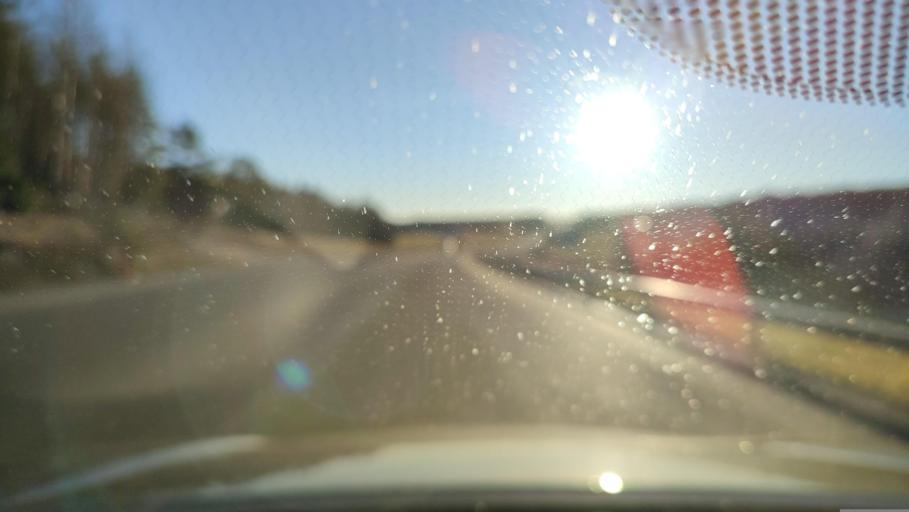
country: SE
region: Vaesterbotten
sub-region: Robertsfors Kommun
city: Robertsfors
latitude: 64.2150
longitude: 21.0167
